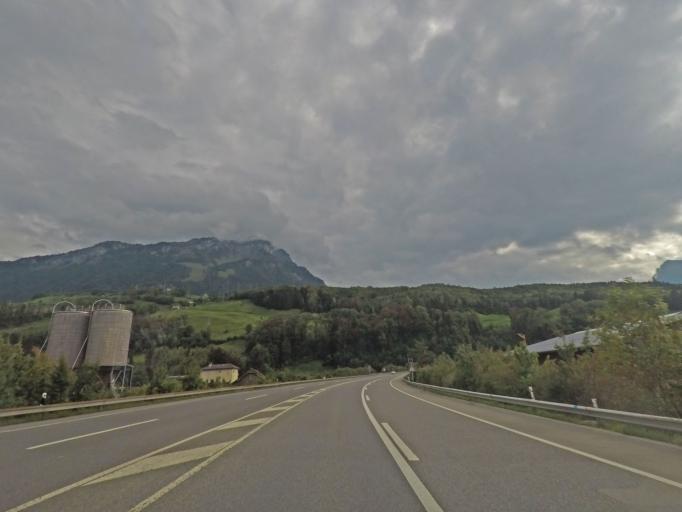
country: CH
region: Schwyz
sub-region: Bezirk Schwyz
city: Ingenbohl
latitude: 47.0009
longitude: 8.6226
